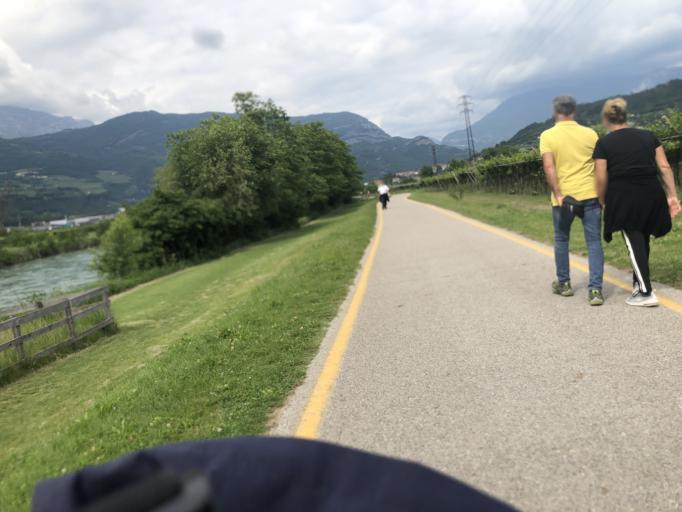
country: IT
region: Trentino-Alto Adige
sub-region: Provincia di Trento
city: Nogaredo
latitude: 45.8995
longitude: 11.0285
